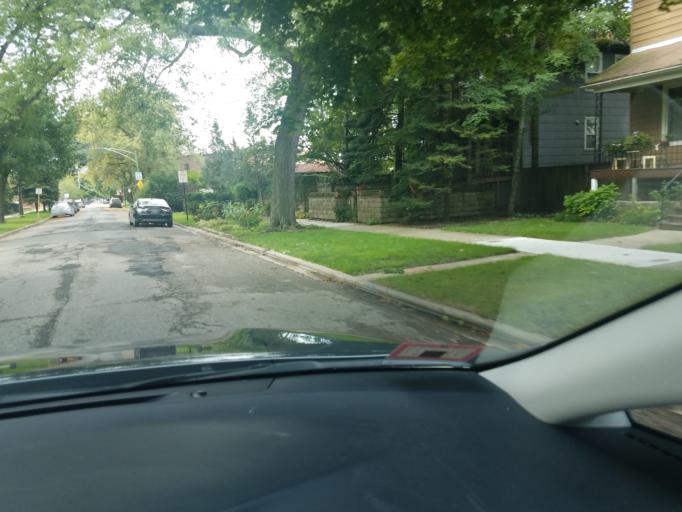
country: US
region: Illinois
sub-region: Cook County
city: Lincolnwood
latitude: 41.9600
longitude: -87.7266
